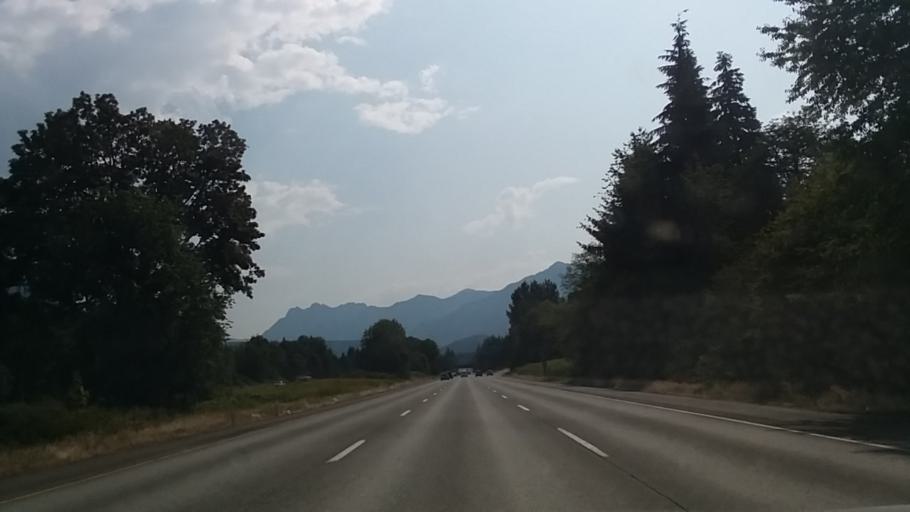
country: US
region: Washington
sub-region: King County
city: Riverbend
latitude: 47.4732
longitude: -121.7674
